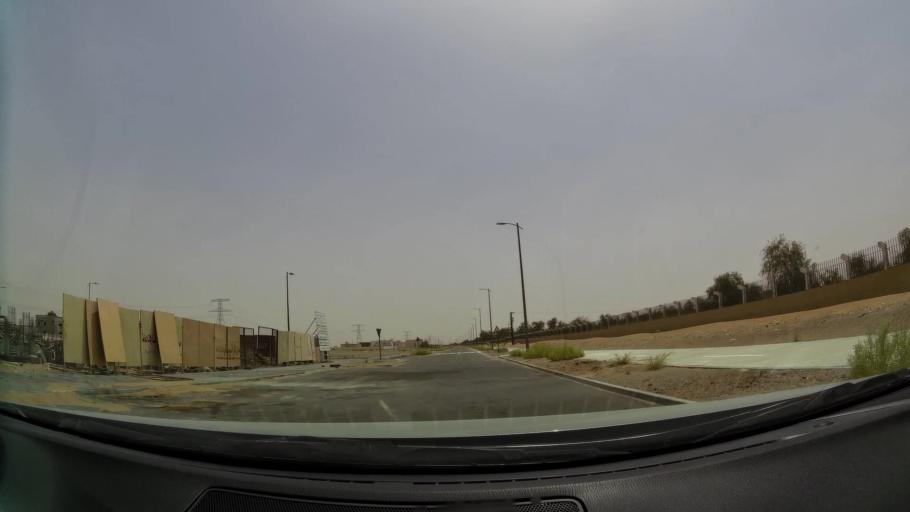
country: AE
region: Abu Dhabi
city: Al Ain
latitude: 24.1579
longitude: 55.6376
